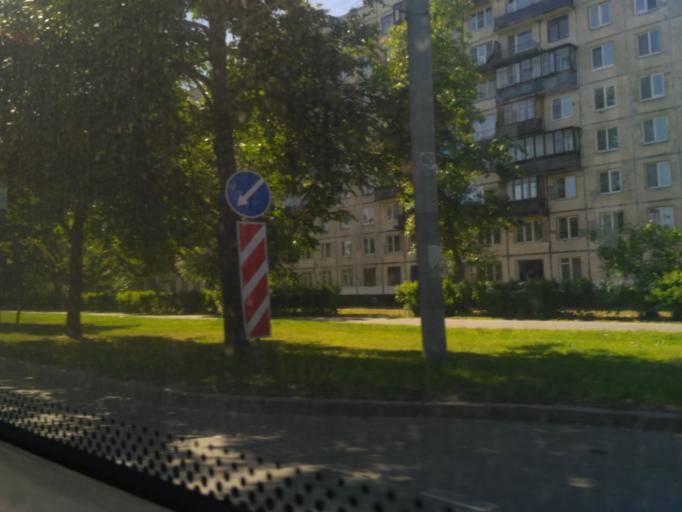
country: RU
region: Leningrad
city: Kalininskiy
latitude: 59.9639
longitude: 30.4199
